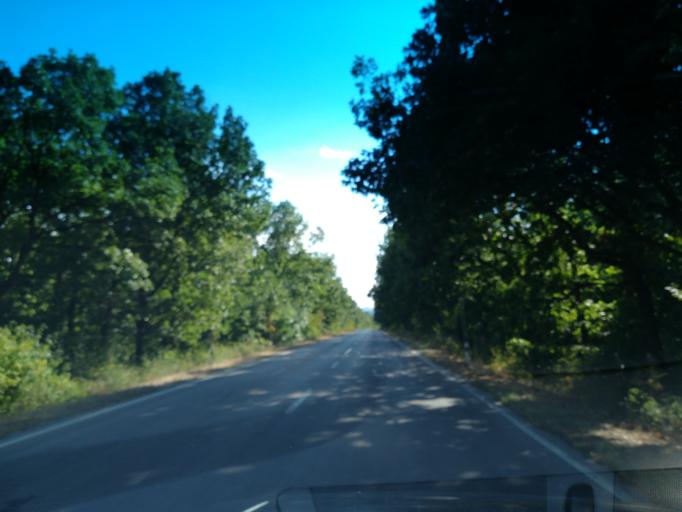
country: BG
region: Khaskovo
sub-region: Obshtina Mineralni Bani
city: Mineralni Bani
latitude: 41.9933
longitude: 25.3606
